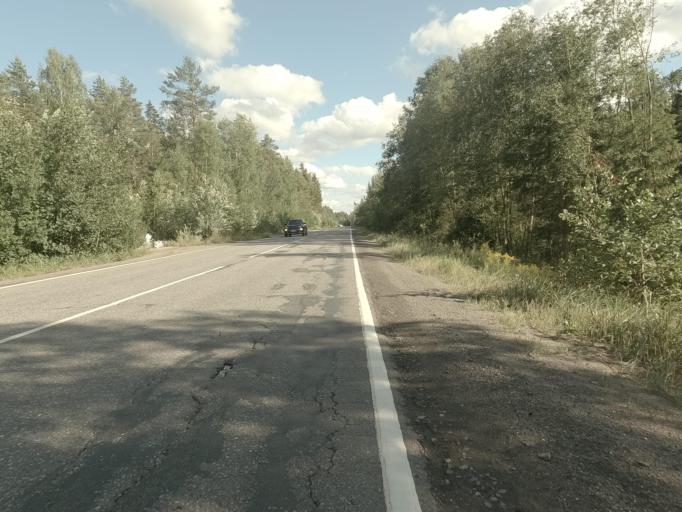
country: RU
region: Leningrad
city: Borisova Griva
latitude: 59.9904
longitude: 30.8839
